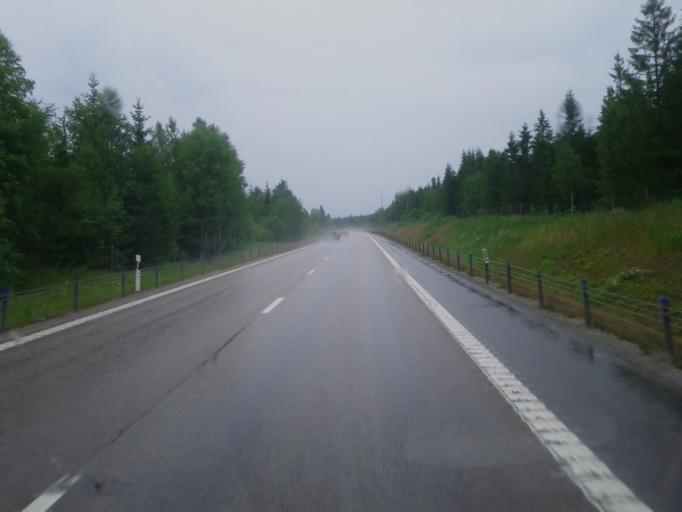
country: SE
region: Uppsala
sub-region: Tierps Kommun
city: Tierp
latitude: 60.3939
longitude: 17.4764
